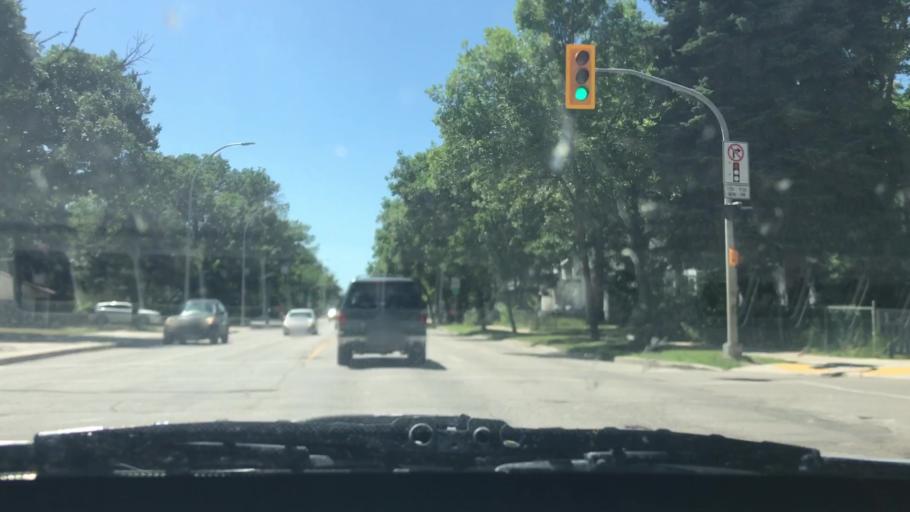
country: CA
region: Manitoba
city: Winnipeg
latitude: 49.8562
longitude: -97.1409
